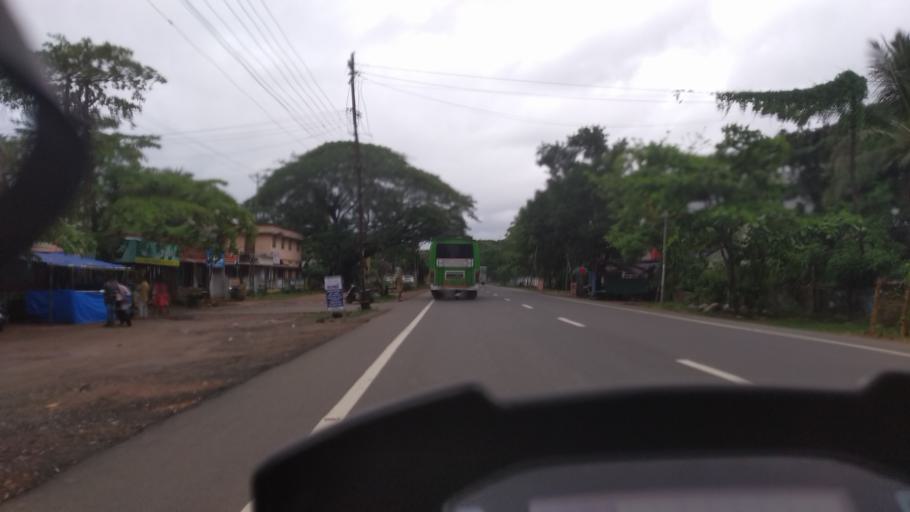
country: IN
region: Kerala
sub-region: Alappuzha
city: Alleppey
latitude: 9.4534
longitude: 76.3412
